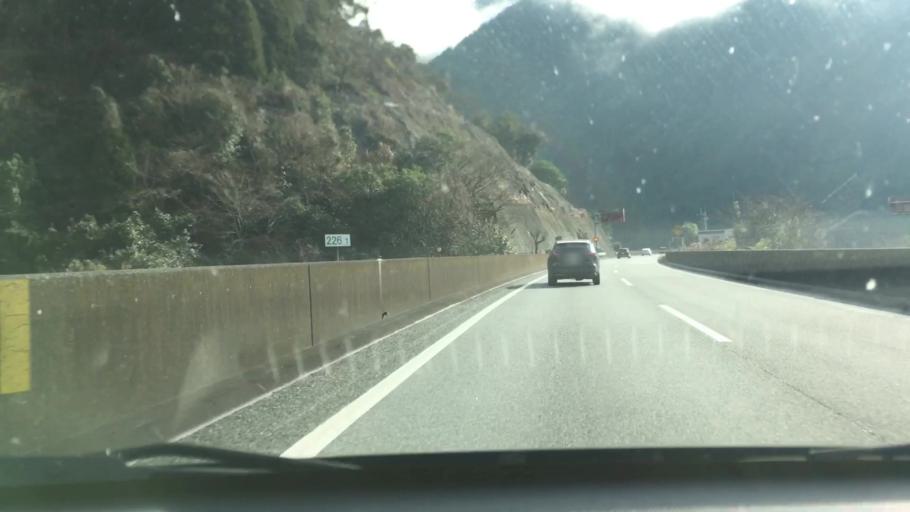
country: JP
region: Kumamoto
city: Yatsushiro
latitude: 32.4277
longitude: 130.7025
